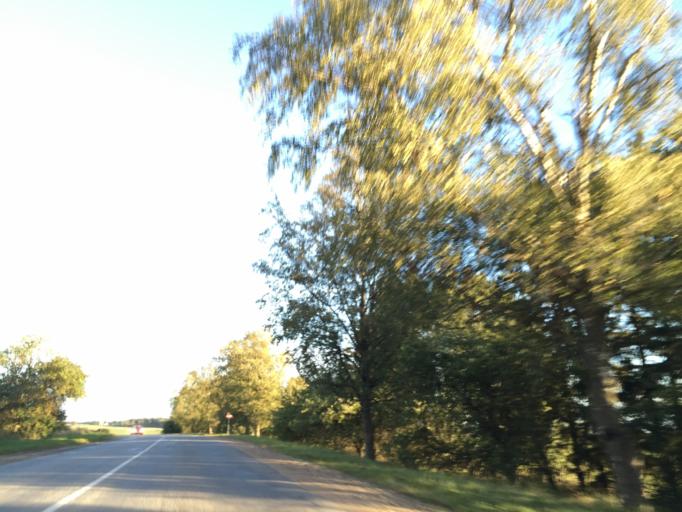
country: LV
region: Saldus Rajons
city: Saldus
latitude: 56.7193
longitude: 22.3884
